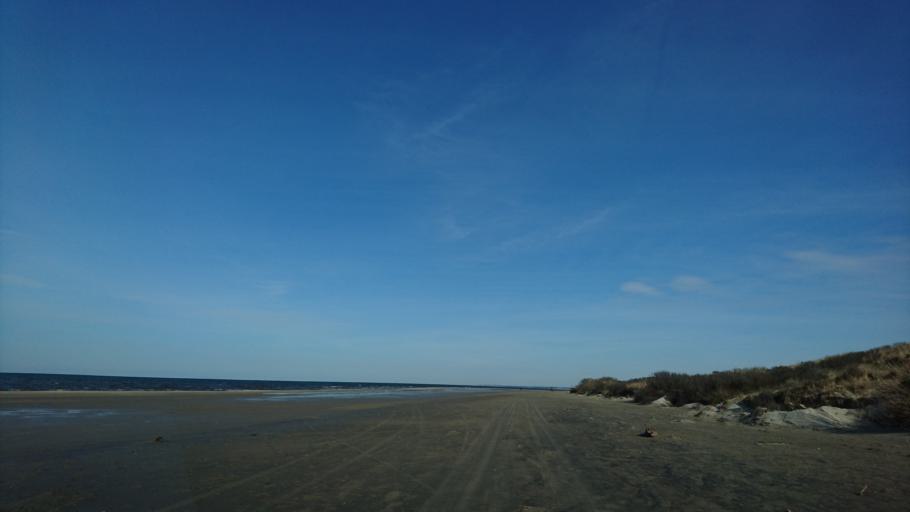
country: DK
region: North Denmark
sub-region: Hjorring Kommune
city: Hirtshals
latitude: 57.5905
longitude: 10.0427
